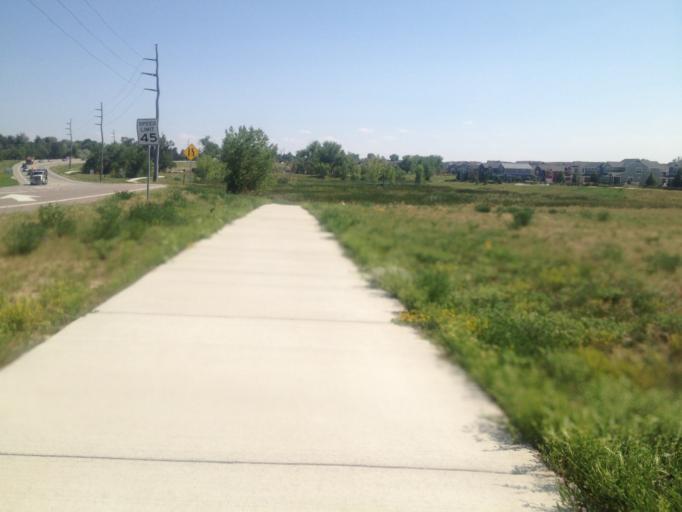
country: US
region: Colorado
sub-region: Boulder County
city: Louisville
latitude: 39.9996
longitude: -105.1312
